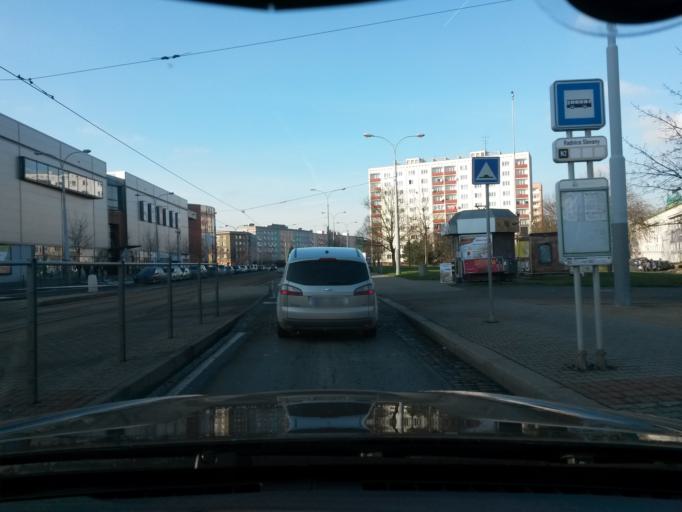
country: CZ
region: Plzensky
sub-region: Okres Plzen-Mesto
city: Pilsen
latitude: 49.7322
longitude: 13.4026
